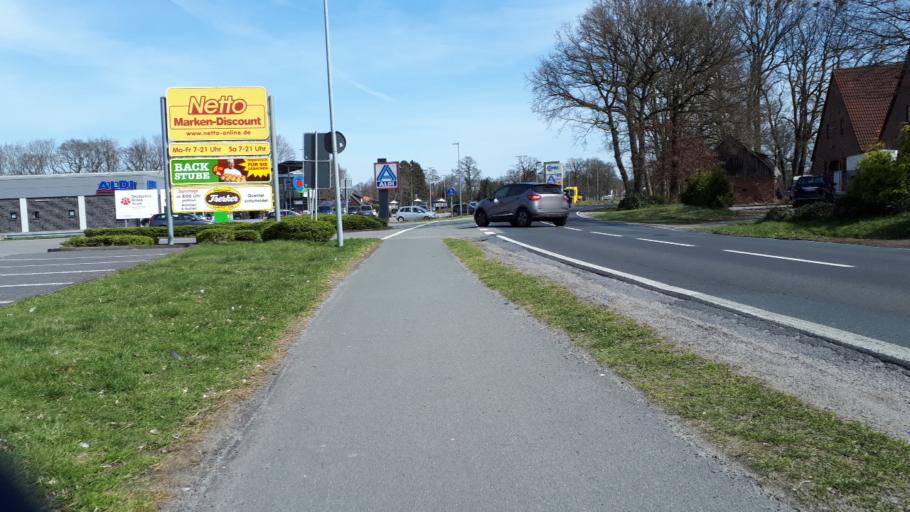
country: DE
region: Lower Saxony
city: Garrel
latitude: 52.9607
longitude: 8.0276
